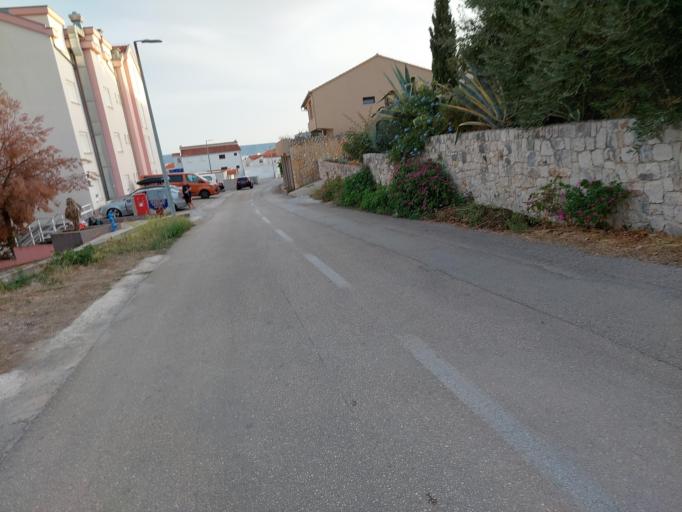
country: HR
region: Splitsko-Dalmatinska
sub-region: Grad Trogir
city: Trogir
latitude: 43.4952
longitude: 16.2710
